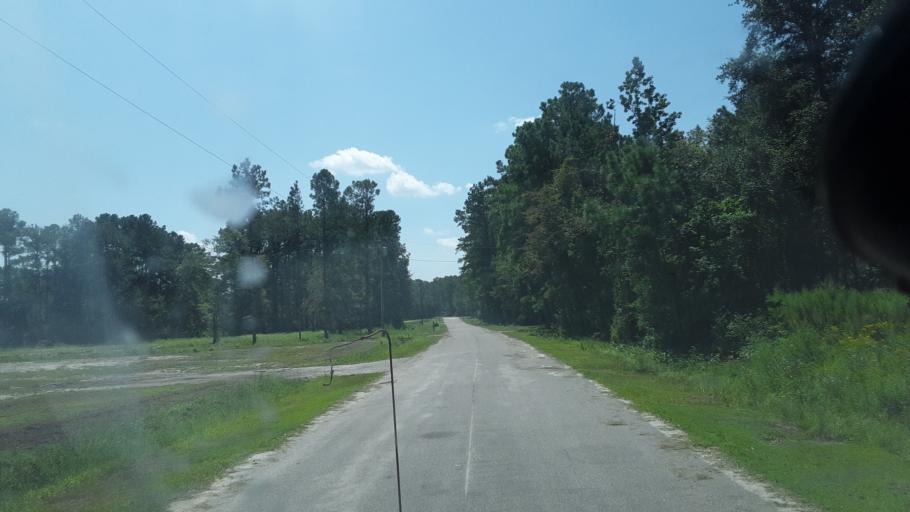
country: US
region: South Carolina
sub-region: Horry County
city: Forestbrook
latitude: 33.8397
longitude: -78.8624
